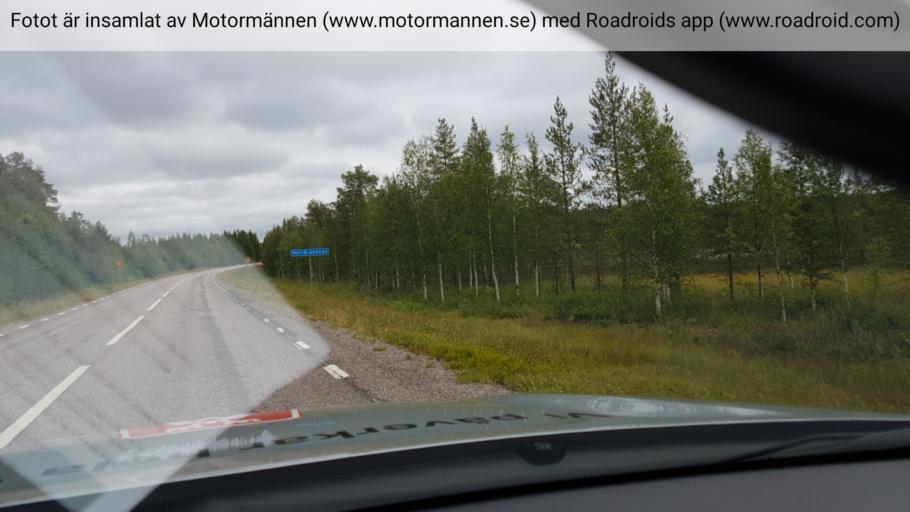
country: SE
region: Norrbotten
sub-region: Gallivare Kommun
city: Gaellivare
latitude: 67.0620
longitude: 21.2670
